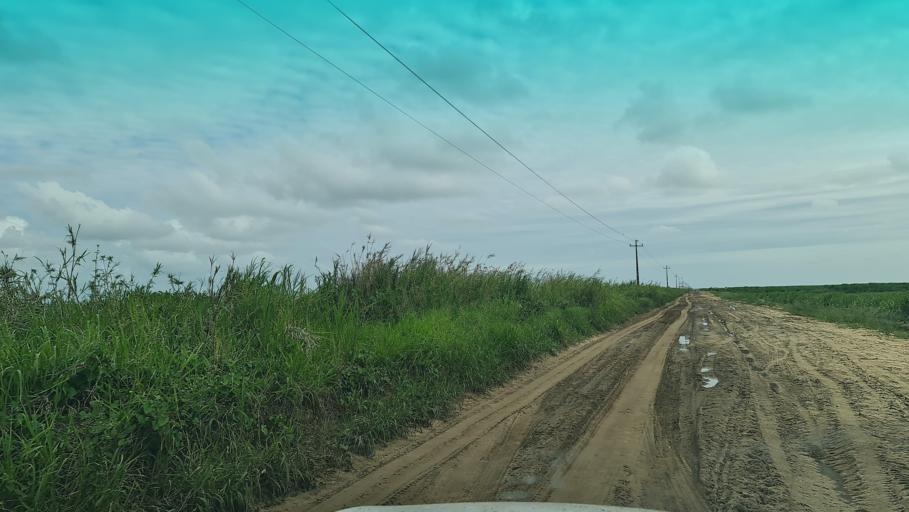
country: MZ
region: Maputo
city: Manhica
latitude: -25.4492
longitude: 32.8394
